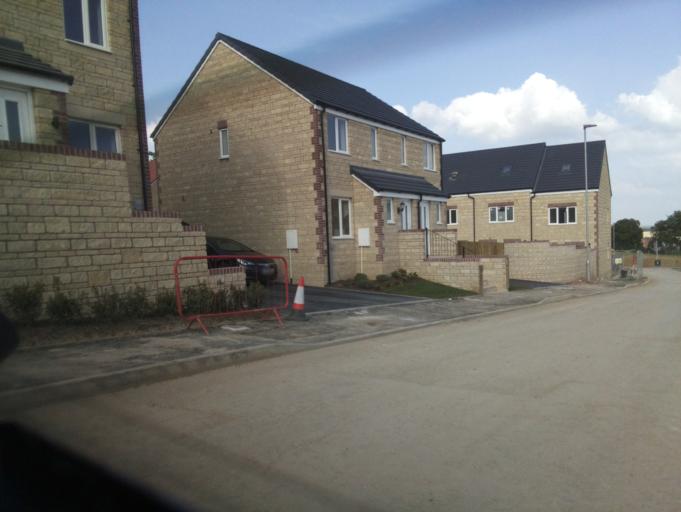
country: GB
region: England
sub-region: Wiltshire
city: Chippenham
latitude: 51.4744
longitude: -2.1218
